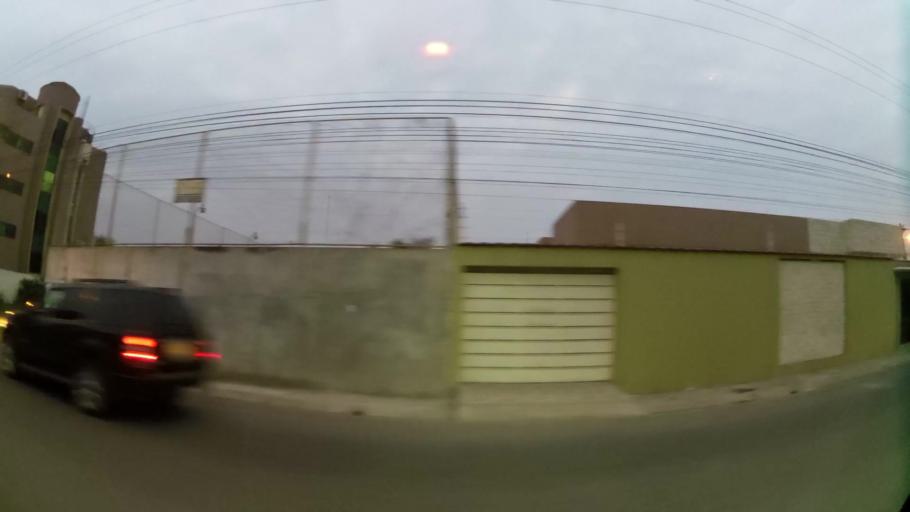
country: EC
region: El Oro
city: Machala
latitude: -3.2625
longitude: -79.9398
